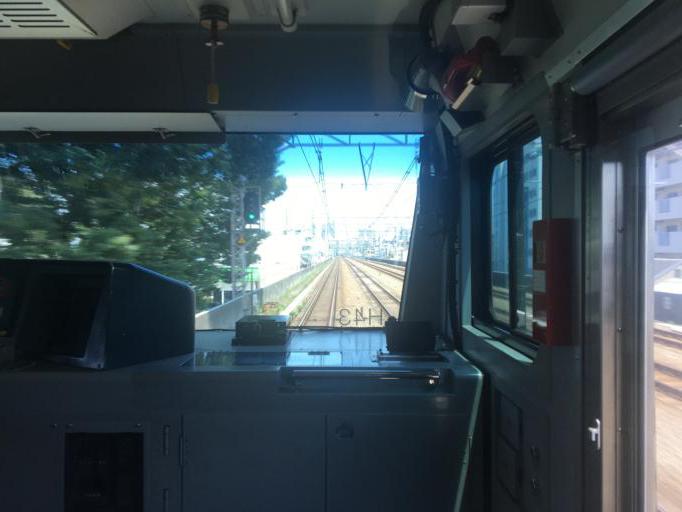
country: JP
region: Tokyo
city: Musashino
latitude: 35.7041
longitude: 139.6061
